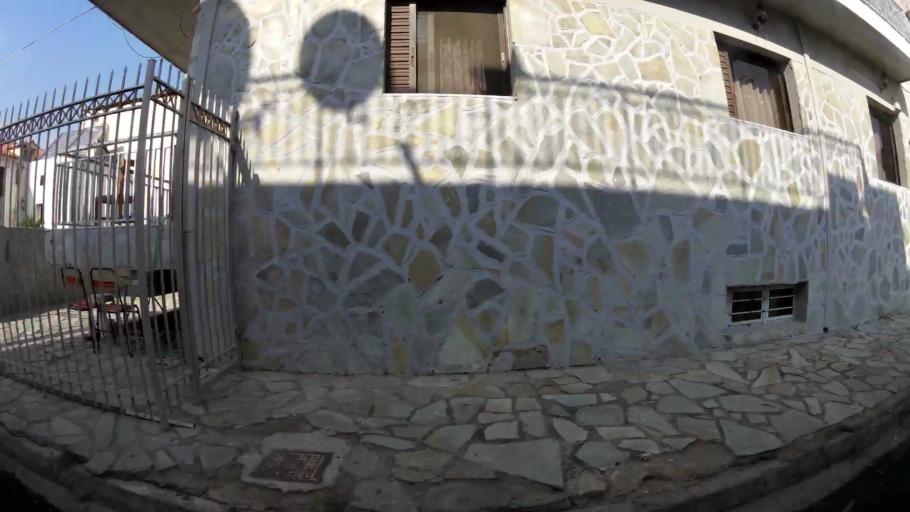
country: GR
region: Attica
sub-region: Nomarchia Dytikis Attikis
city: Zefyri
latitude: 38.0748
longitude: 23.7173
